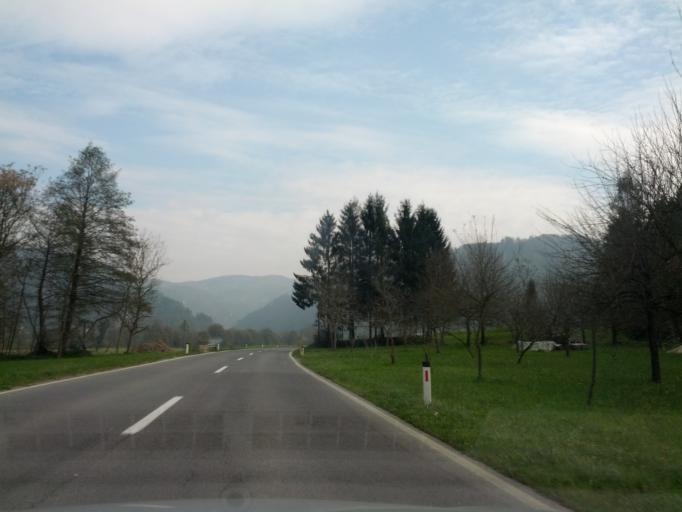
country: SI
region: Smartno pri Litiji
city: Smartno pri Litiji
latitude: 46.0826
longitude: 14.8800
